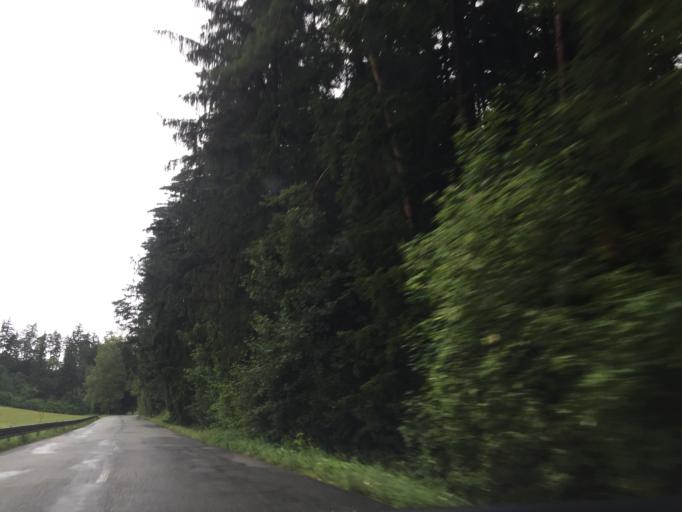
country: CZ
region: South Moravian
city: Ostrov u Macochy
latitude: 49.3895
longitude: 16.7694
